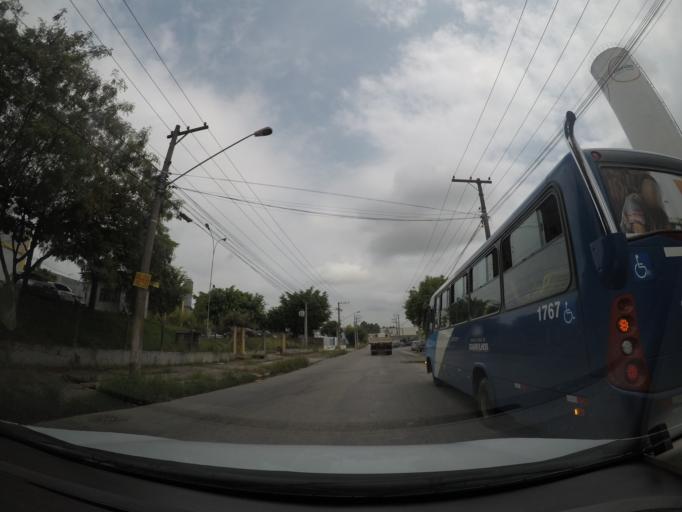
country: BR
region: Sao Paulo
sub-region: Itaquaquecetuba
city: Itaquaquecetuba
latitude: -23.4262
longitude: -46.3947
